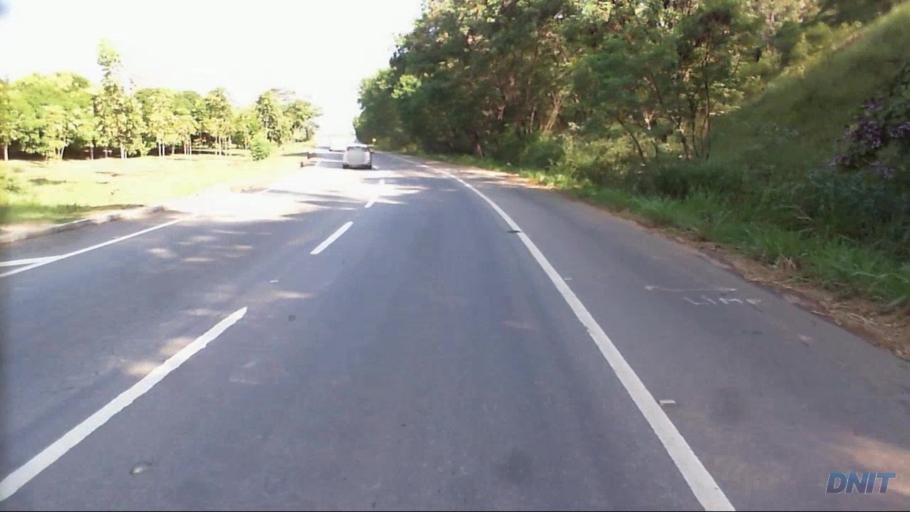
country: BR
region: Minas Gerais
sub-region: Coronel Fabriciano
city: Coronel Fabriciano
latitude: -19.5136
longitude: -42.5763
